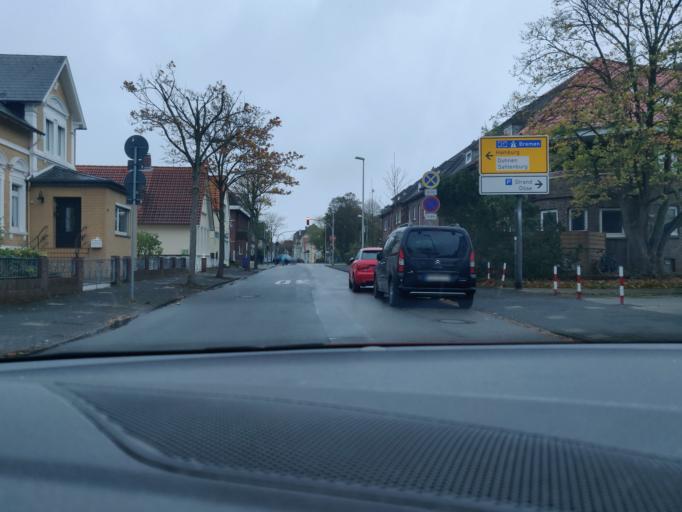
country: DE
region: Lower Saxony
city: Cuxhaven
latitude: 53.8848
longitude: 8.6655
